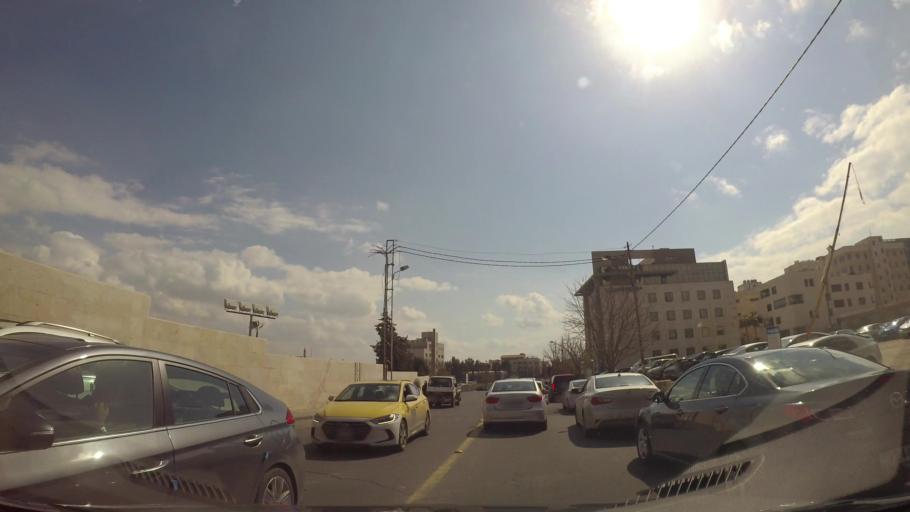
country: JO
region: Amman
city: Amman
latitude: 31.9672
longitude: 35.8959
